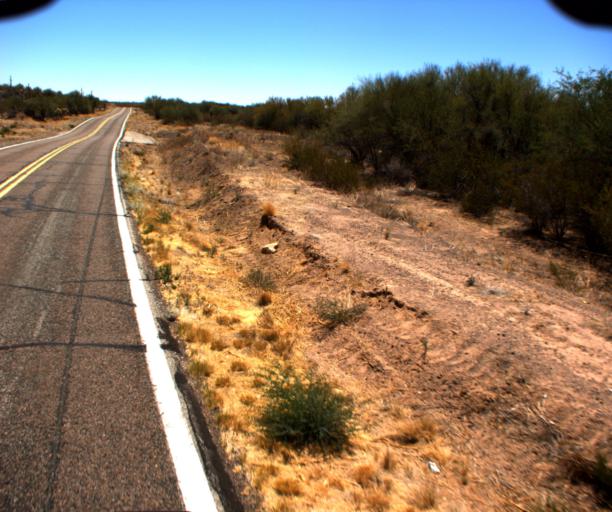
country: US
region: Arizona
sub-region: Pima County
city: Ajo
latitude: 32.2228
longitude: -112.6843
